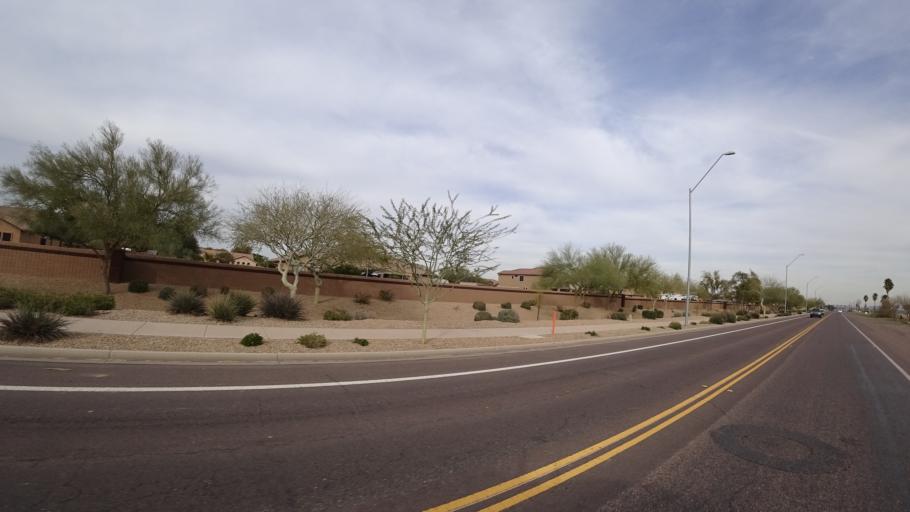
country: US
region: Arizona
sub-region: Maricopa County
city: El Mirage
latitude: 33.5803
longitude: -112.3648
